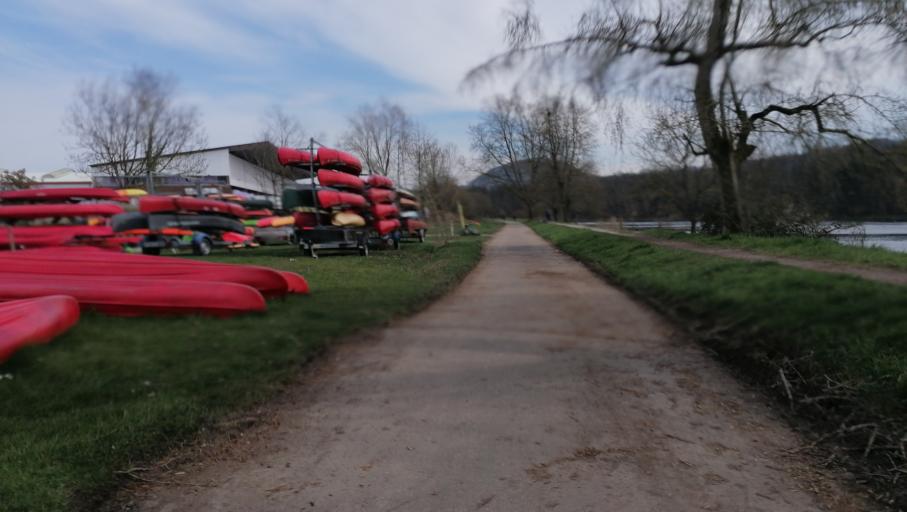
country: DE
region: Baden-Wuerttemberg
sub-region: Freiburg Region
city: Murg
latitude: 47.5536
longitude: 8.0122
